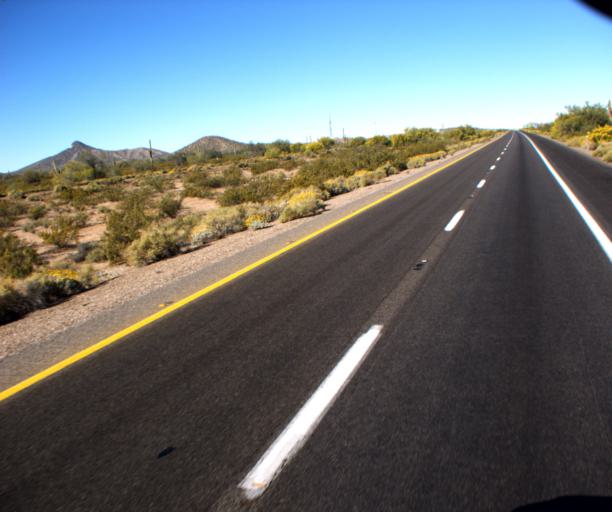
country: US
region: Arizona
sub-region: Pinal County
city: Maricopa
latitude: 32.8343
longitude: -112.1197
